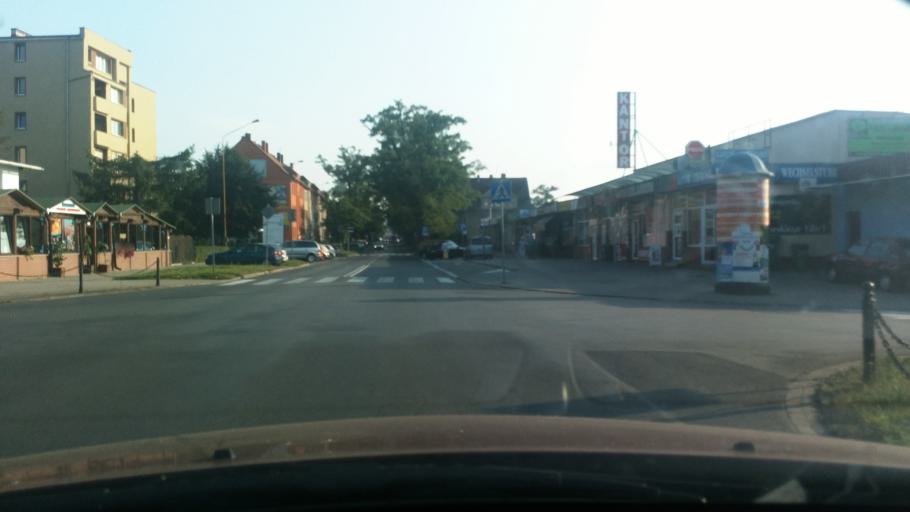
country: PL
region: Lower Silesian Voivodeship
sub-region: Powiat zgorzelecki
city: Zgorzelec
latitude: 51.1570
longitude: 15.0075
